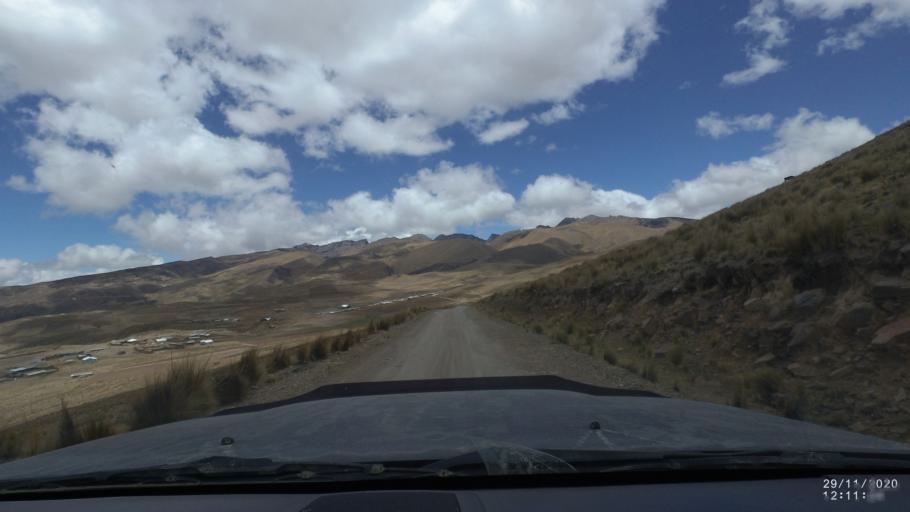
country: BO
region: Cochabamba
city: Cochabamba
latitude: -17.1195
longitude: -66.3054
